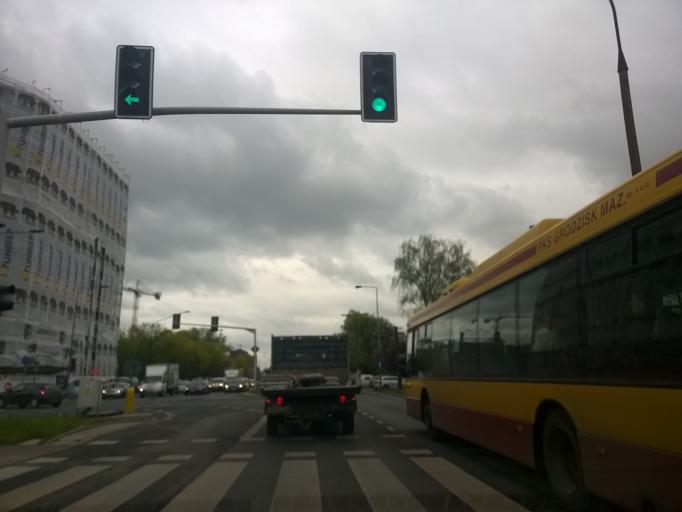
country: PL
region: Masovian Voivodeship
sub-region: Warszawa
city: Mokotow
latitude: 52.1784
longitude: 21.0273
